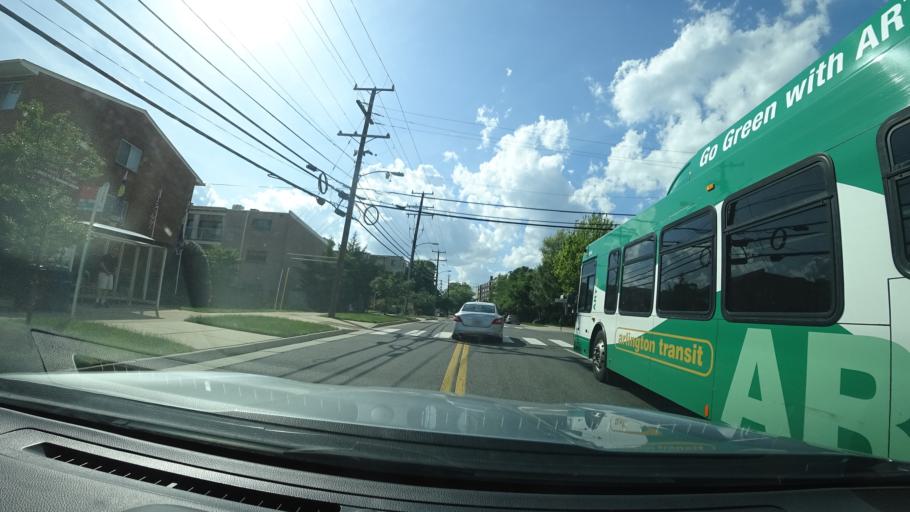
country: US
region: Virginia
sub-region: Arlington County
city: Arlington
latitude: 38.8975
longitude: -77.1151
